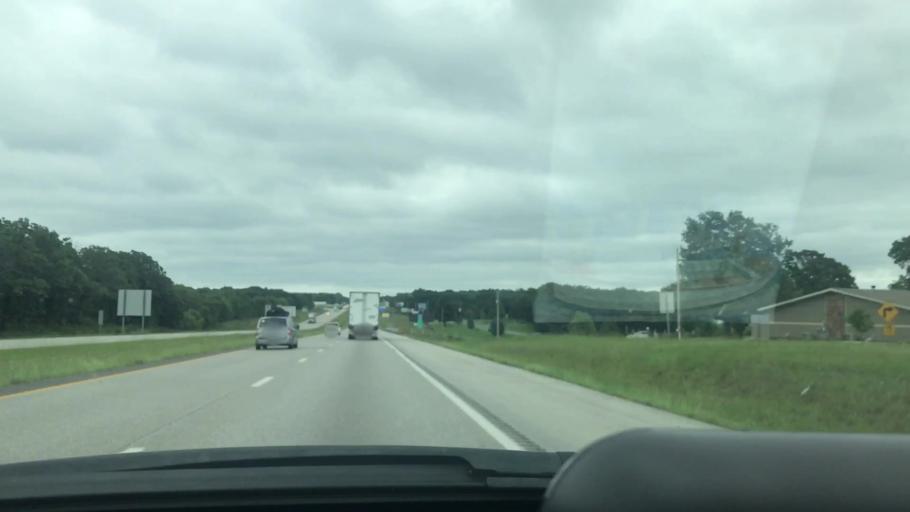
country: US
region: Kansas
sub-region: Cherokee County
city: Galena
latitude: 37.0008
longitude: -94.5983
